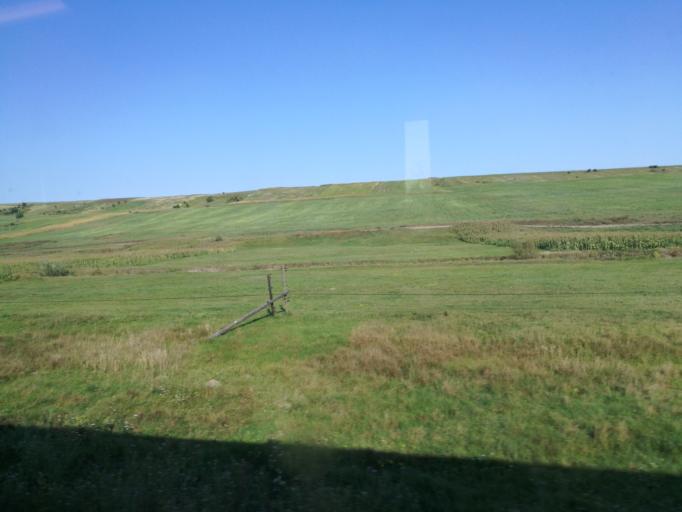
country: RO
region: Vaslui
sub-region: Comuna Rebricea
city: Rebricea
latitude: 46.8616
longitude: 27.5628
